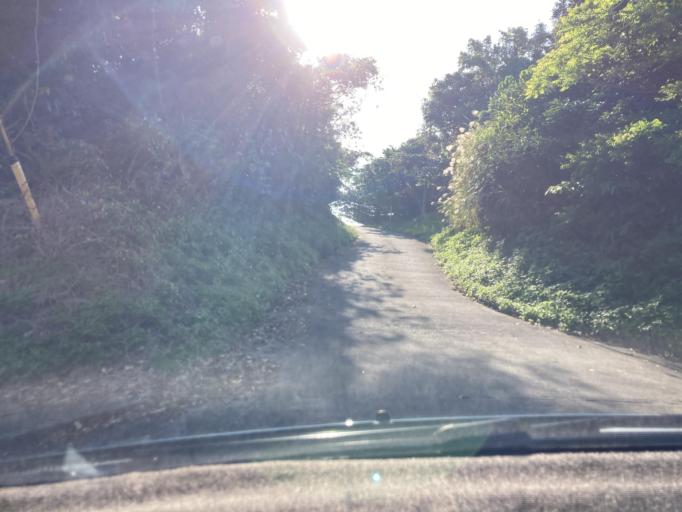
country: JP
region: Okinawa
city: Itoman
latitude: 26.1218
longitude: 127.7494
